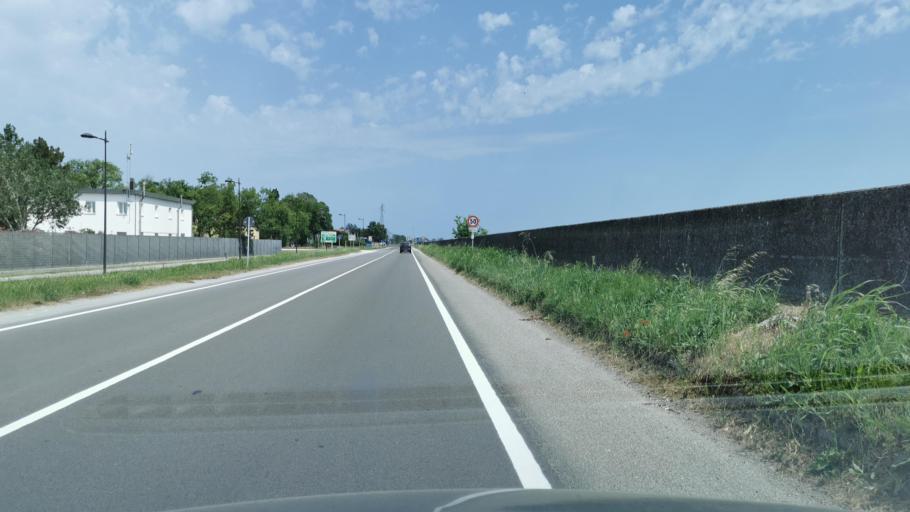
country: IT
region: Emilia-Romagna
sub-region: Provincia di Ferrara
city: Porto Garibaldi
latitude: 44.6775
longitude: 12.2081
